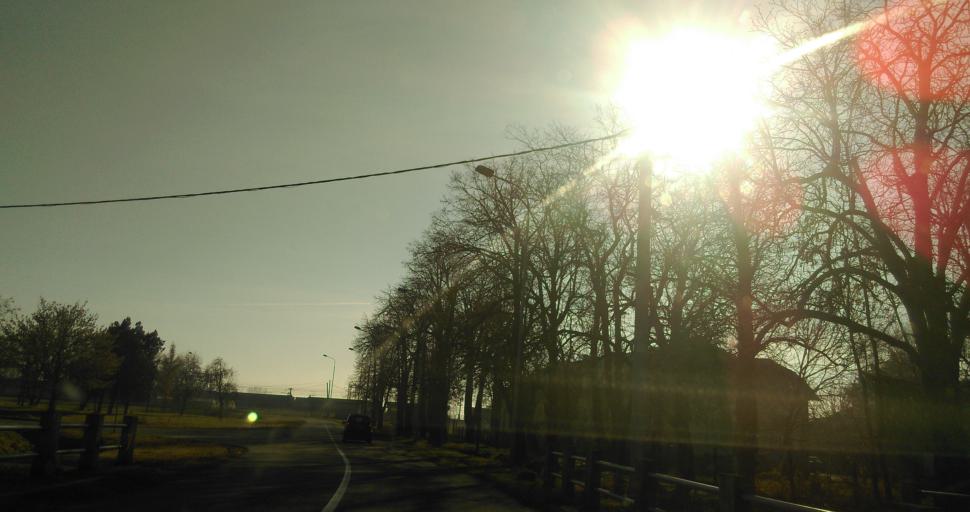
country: RS
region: Autonomna Pokrajina Vojvodina
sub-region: Sremski Okrug
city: Ruma
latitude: 44.9912
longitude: 19.8232
